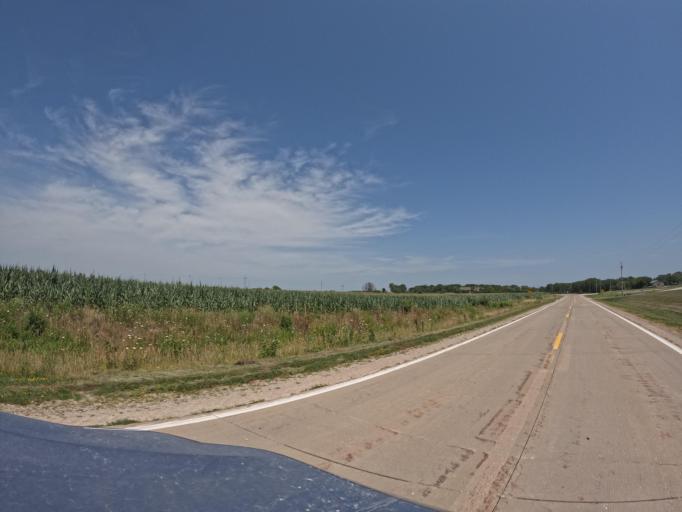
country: US
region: Iowa
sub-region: Henry County
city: Mount Pleasant
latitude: 40.9808
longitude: -91.6152
